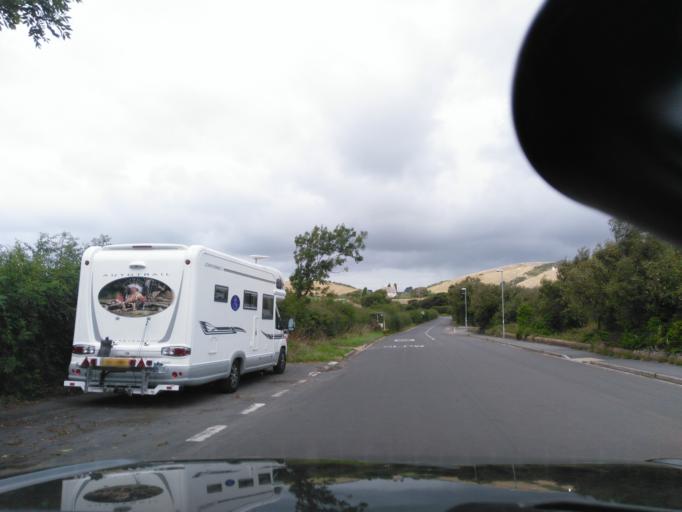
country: GB
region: England
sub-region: Dorset
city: Swanage
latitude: 50.6206
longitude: -1.9653
